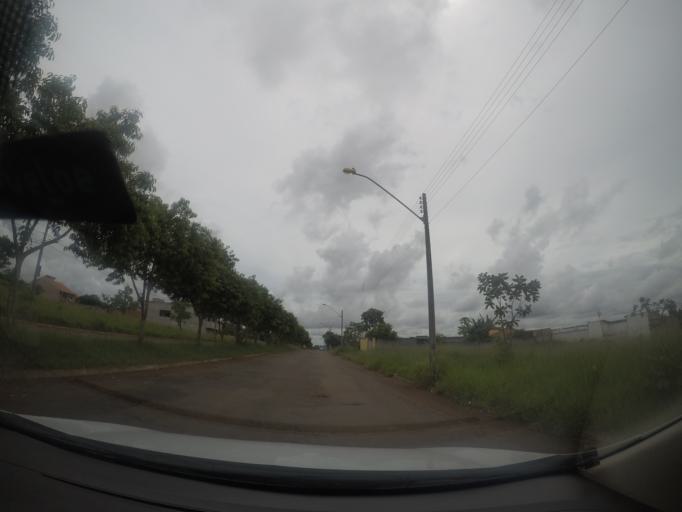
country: BR
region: Goias
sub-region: Trindade
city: Trindade
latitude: -16.6899
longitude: -49.3878
